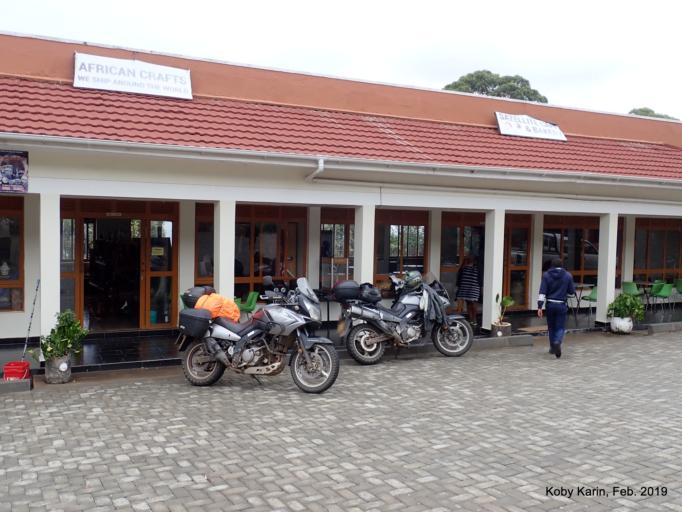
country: UG
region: Western Region
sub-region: Kabale District
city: Kabale
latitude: -1.1527
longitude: 30.1278
